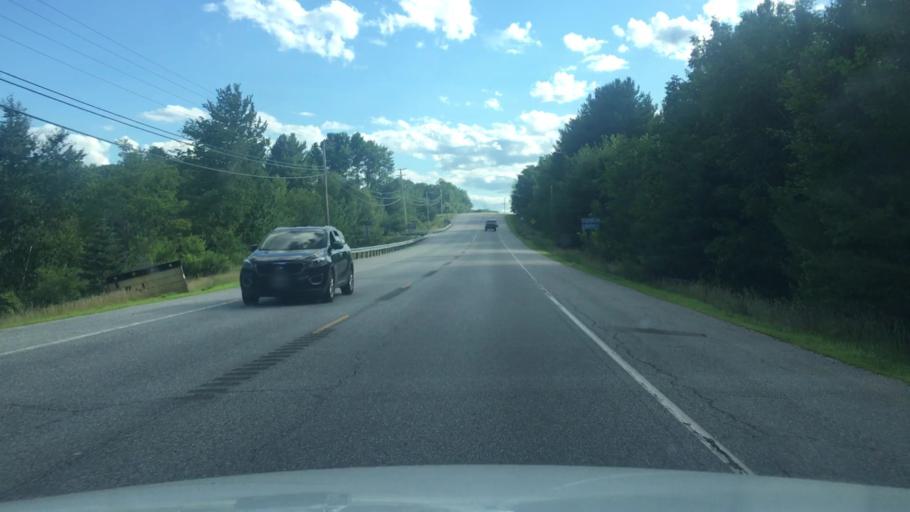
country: US
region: Maine
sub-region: Androscoggin County
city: Livermore Falls
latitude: 44.4462
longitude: -70.2015
